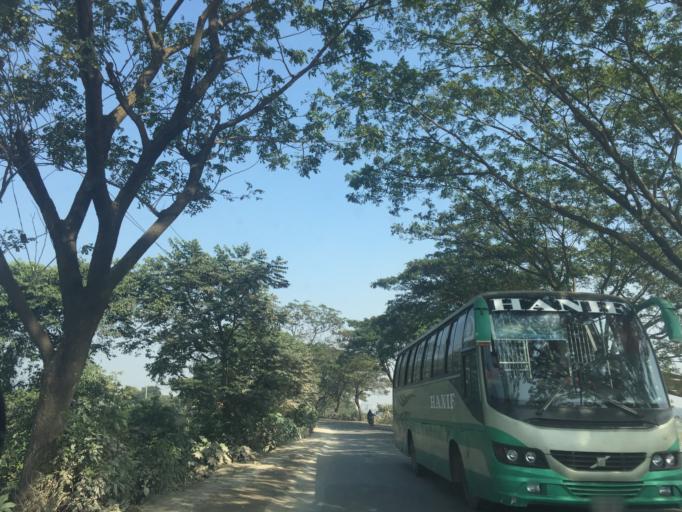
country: BD
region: Dhaka
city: Tungi
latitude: 23.8400
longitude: 90.3421
